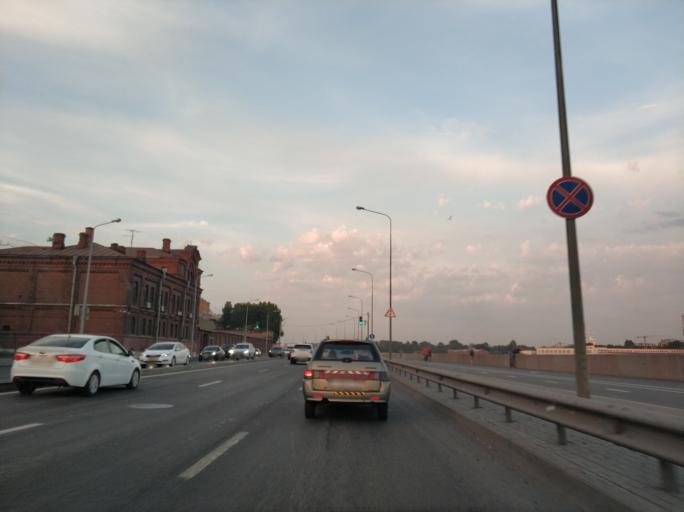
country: RU
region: Leningrad
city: Finlyandskiy
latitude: 59.9528
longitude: 30.3640
